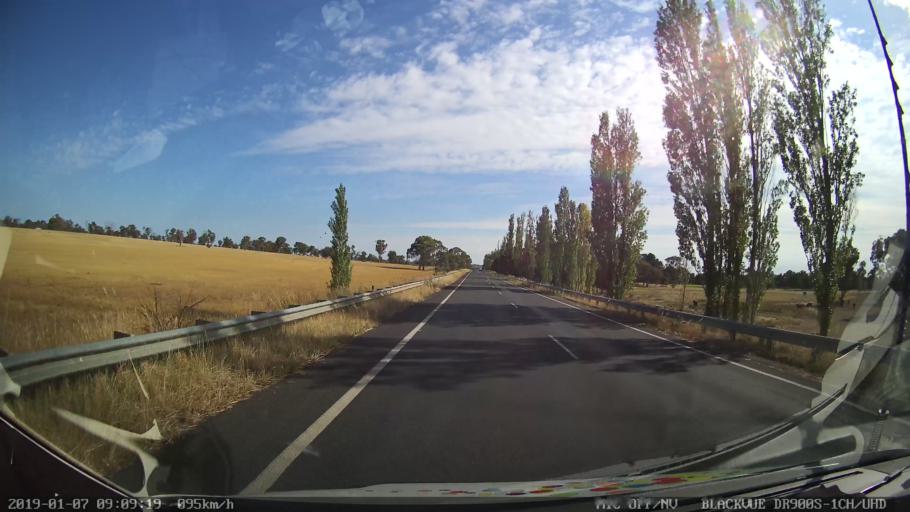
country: AU
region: New South Wales
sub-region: Armidale Dumaresq
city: Armidale
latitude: -30.6593
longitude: 151.4879
